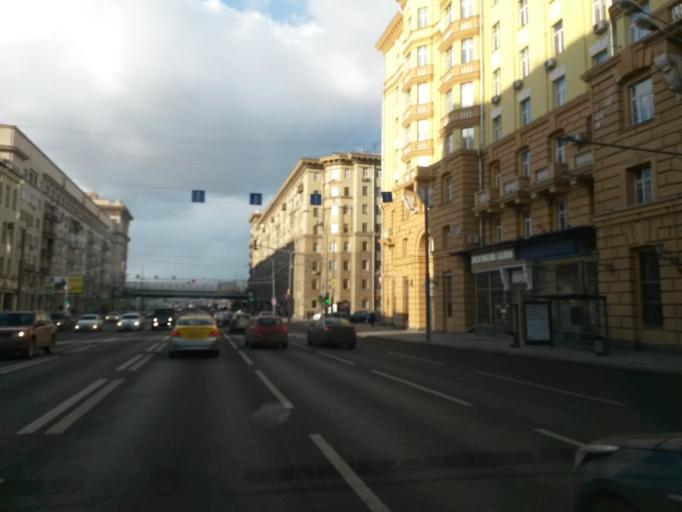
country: RU
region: Moscow
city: Mar'ina Roshcha
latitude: 55.7894
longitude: 37.6349
